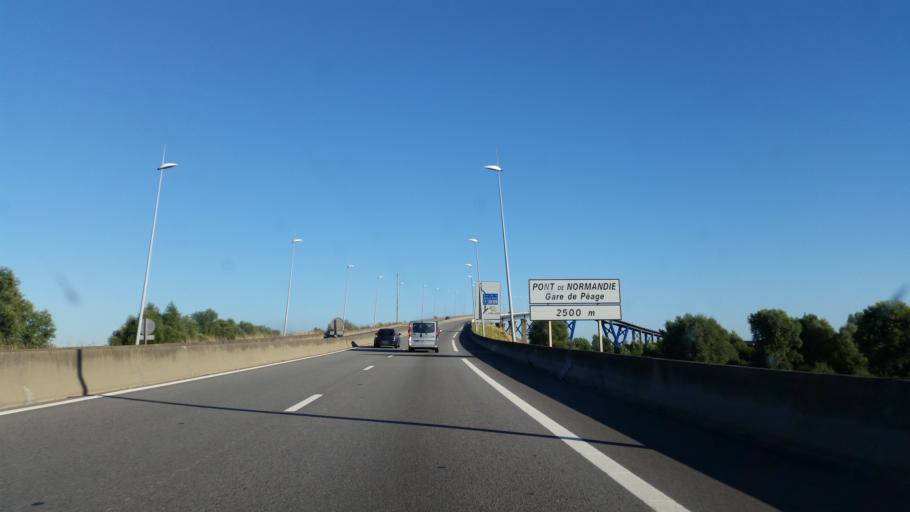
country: FR
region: Haute-Normandie
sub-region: Departement de la Seine-Maritime
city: Rogerville
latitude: 49.4730
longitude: 0.2705
